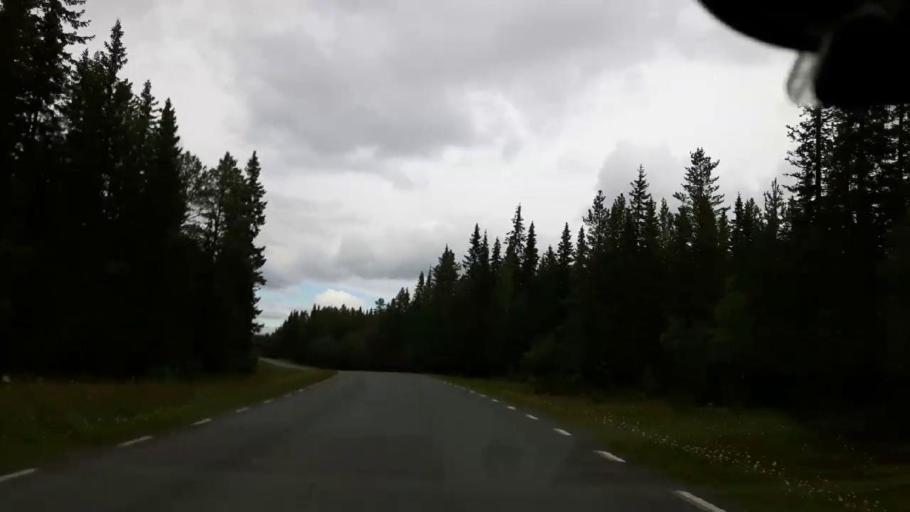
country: SE
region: Jaemtland
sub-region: Krokoms Kommun
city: Valla
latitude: 63.5570
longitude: 13.8505
